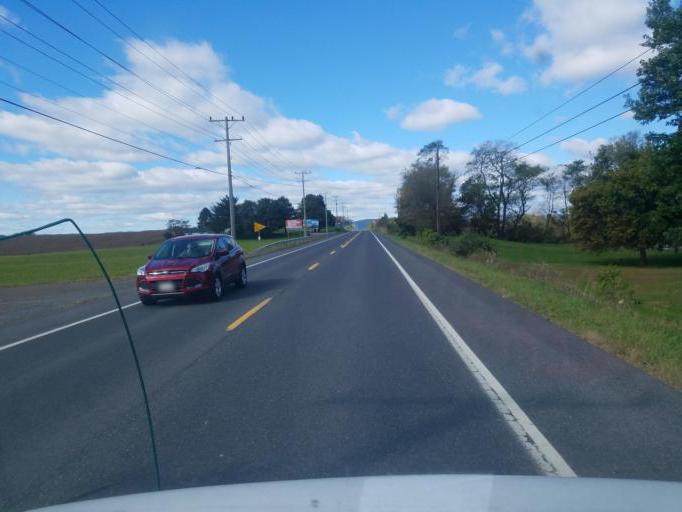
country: US
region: Pennsylvania
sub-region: Franklin County
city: Mercersburg
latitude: 39.8020
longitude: -77.8522
